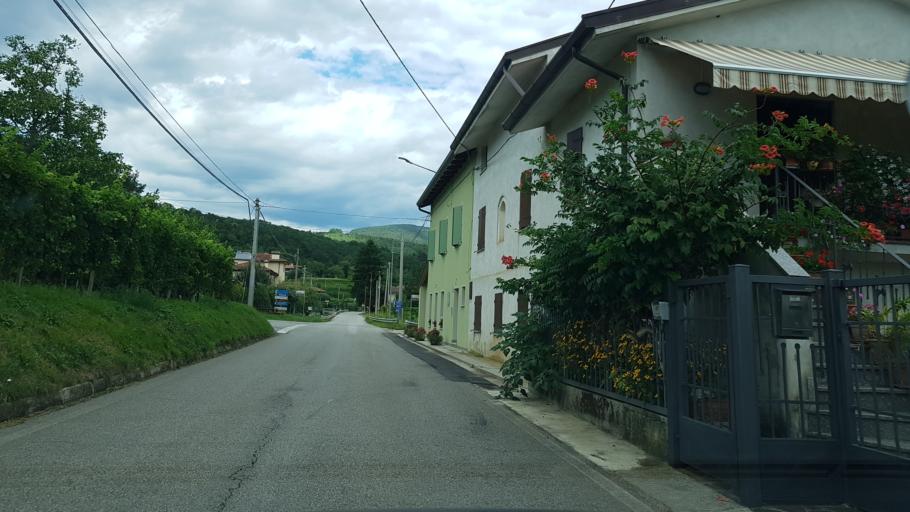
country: IT
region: Friuli Venezia Giulia
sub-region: Provincia di Udine
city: Prepotto
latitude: 46.0519
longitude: 13.4879
